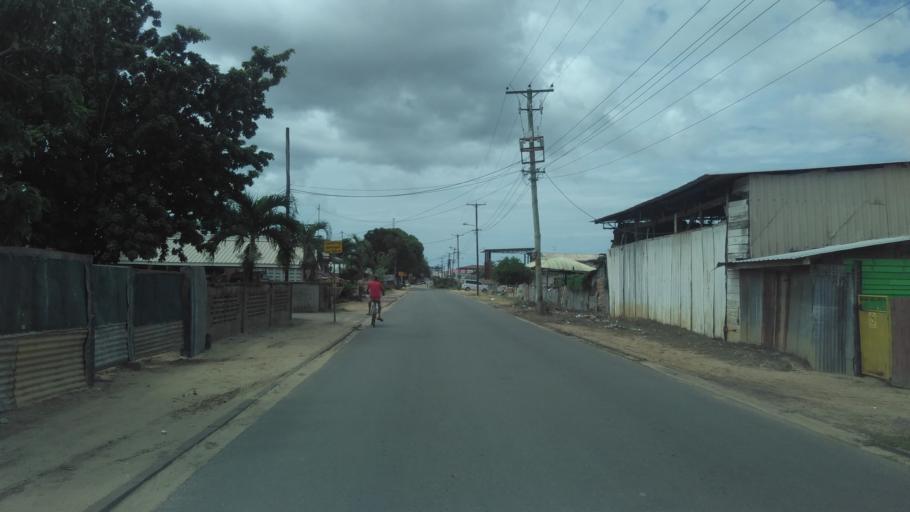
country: SR
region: Paramaribo
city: Paramaribo
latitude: 5.8502
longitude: -55.1294
